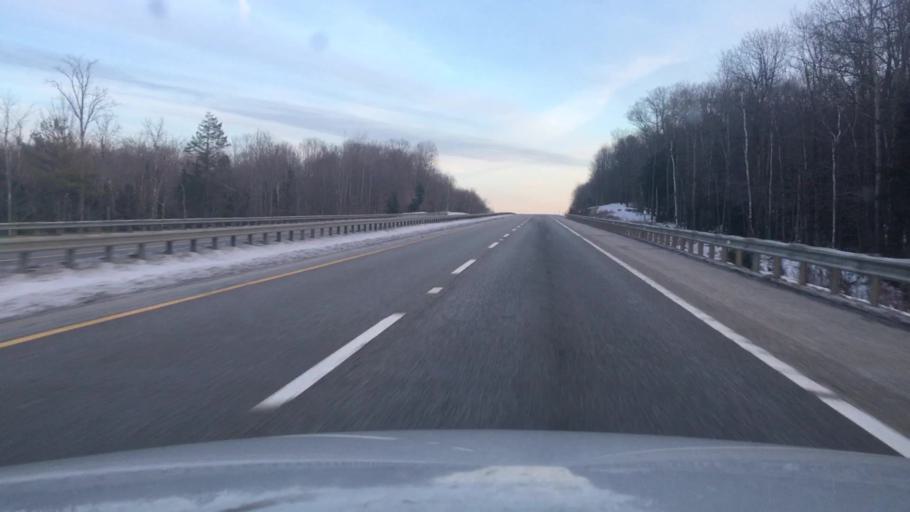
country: US
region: Maine
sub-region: Androscoggin County
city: Sabattus
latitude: 44.1249
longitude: -69.9903
